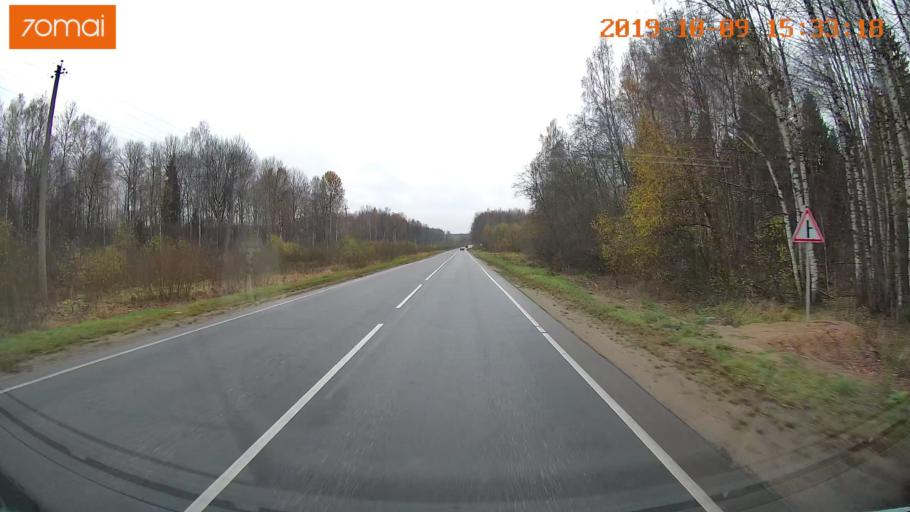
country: RU
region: Kostroma
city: Oktyabr'skiy
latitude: 57.9536
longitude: 41.2643
